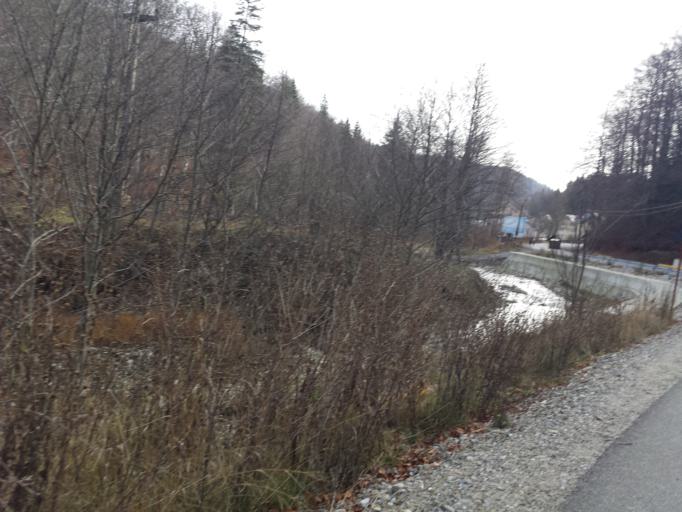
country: RO
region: Prahova
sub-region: Oras Azuga
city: Azuga
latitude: 45.4274
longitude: 25.5373
